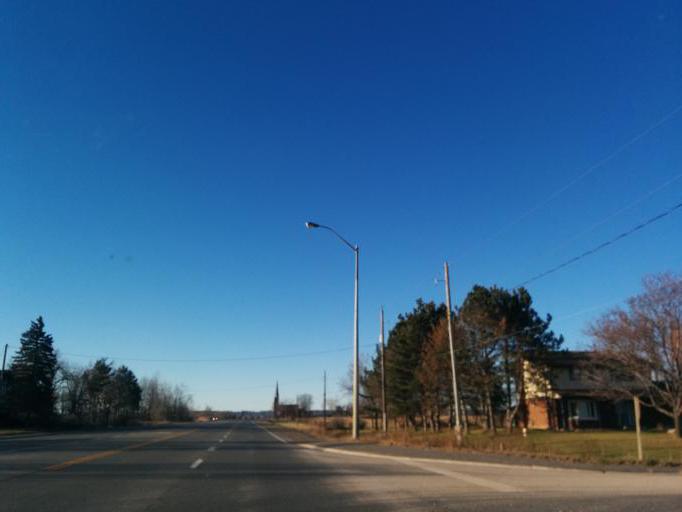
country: CA
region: Ontario
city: Brampton
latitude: 43.7933
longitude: -79.9049
